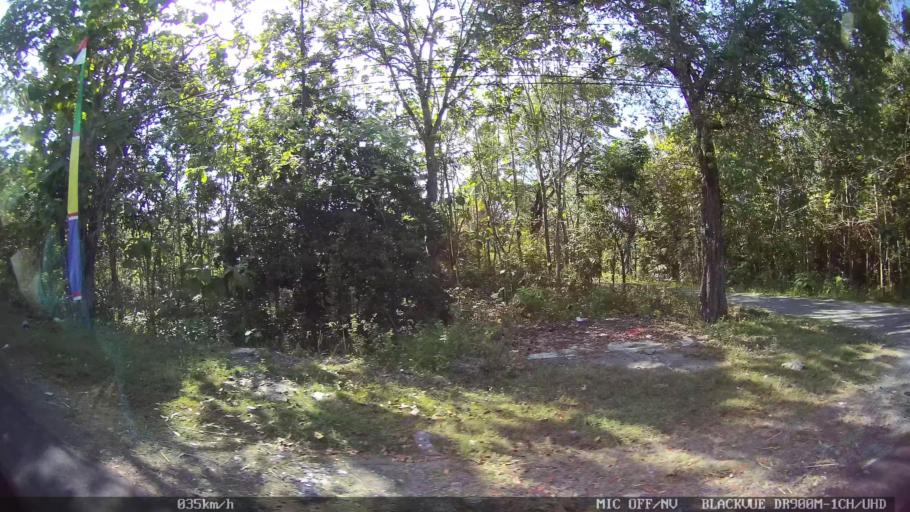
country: ID
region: Daerah Istimewa Yogyakarta
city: Kasihan
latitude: -7.8237
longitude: 110.2919
